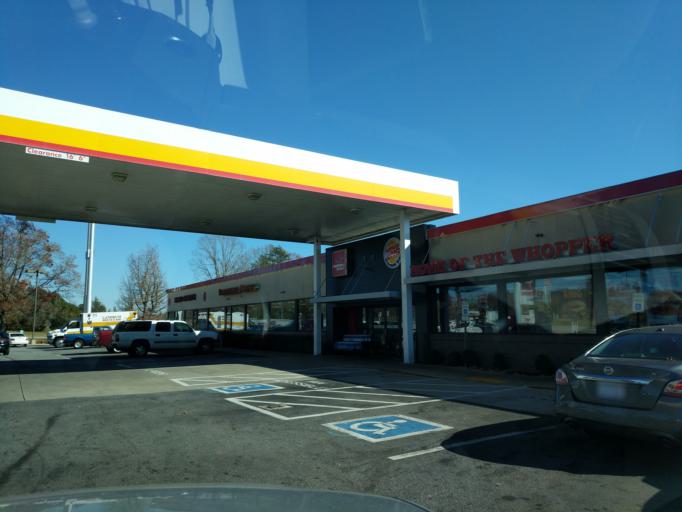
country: US
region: South Carolina
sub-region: Spartanburg County
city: Landrum
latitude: 35.1821
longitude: -82.1591
